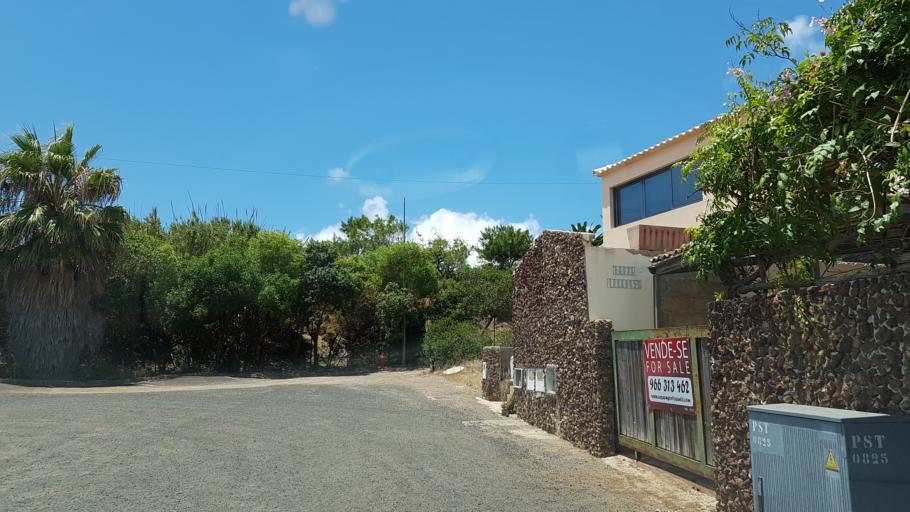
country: PT
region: Madeira
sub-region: Porto Santo
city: Vila de Porto Santo
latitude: 33.0538
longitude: -16.3687
